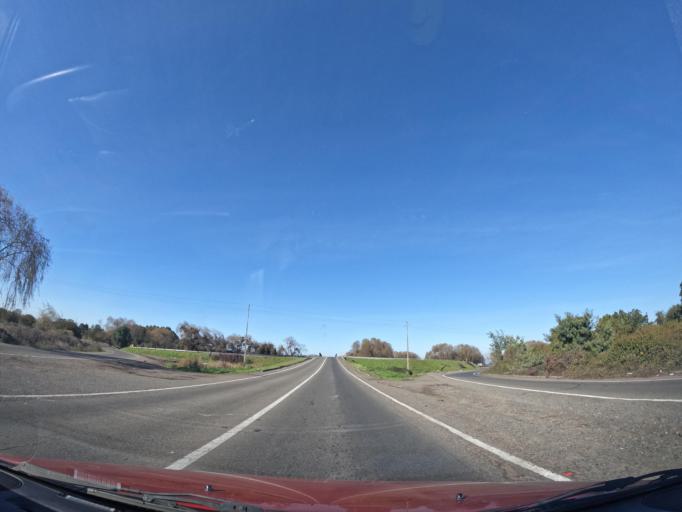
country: CL
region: Maule
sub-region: Provincia de Linares
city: San Javier
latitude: -35.6349
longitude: -71.7009
